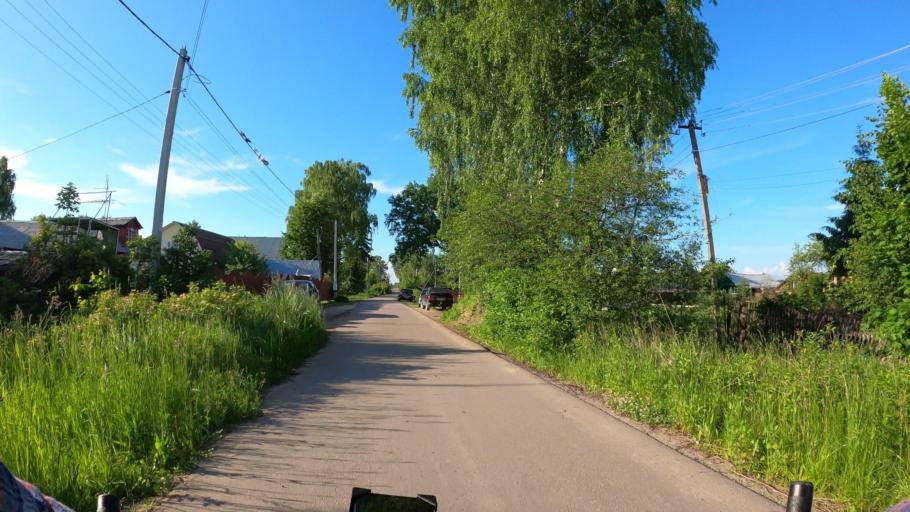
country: RU
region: Moskovskaya
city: Ashitkovo
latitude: 55.4399
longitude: 38.6051
